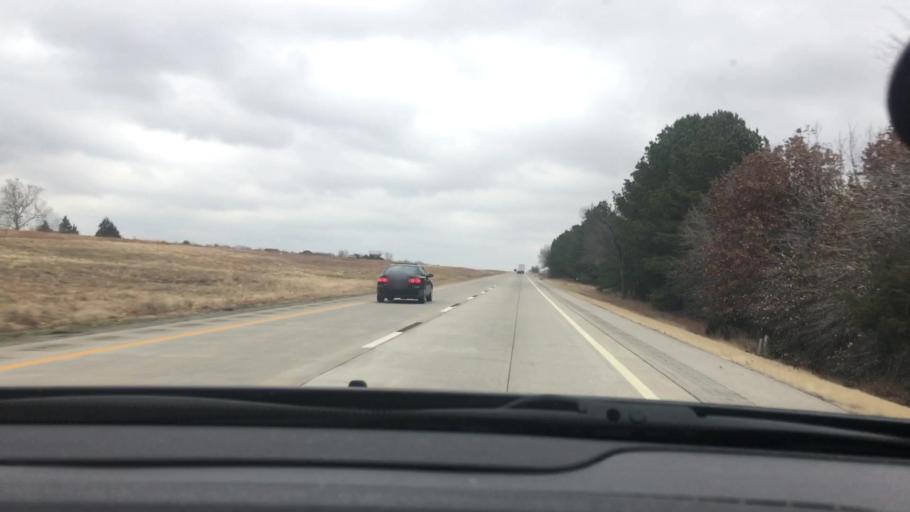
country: US
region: Oklahoma
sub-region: Atoka County
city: Atoka
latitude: 34.1893
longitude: -96.2434
